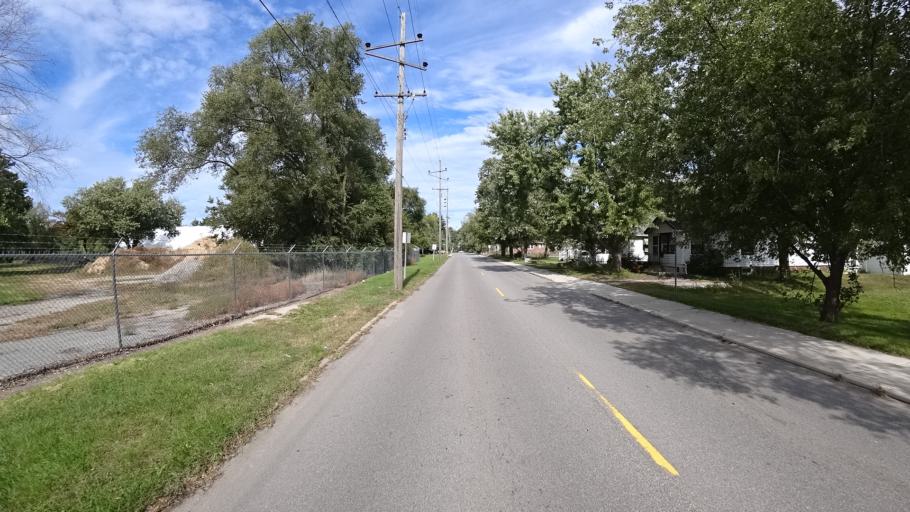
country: US
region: Indiana
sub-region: LaPorte County
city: Trail Creek
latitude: 41.7148
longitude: -86.8698
